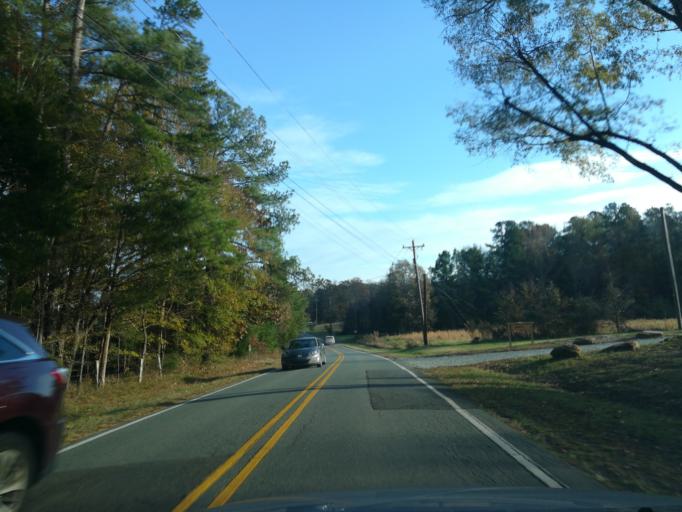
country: US
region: North Carolina
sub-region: Orange County
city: Chapel Hill
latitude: 35.9680
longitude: -79.0049
